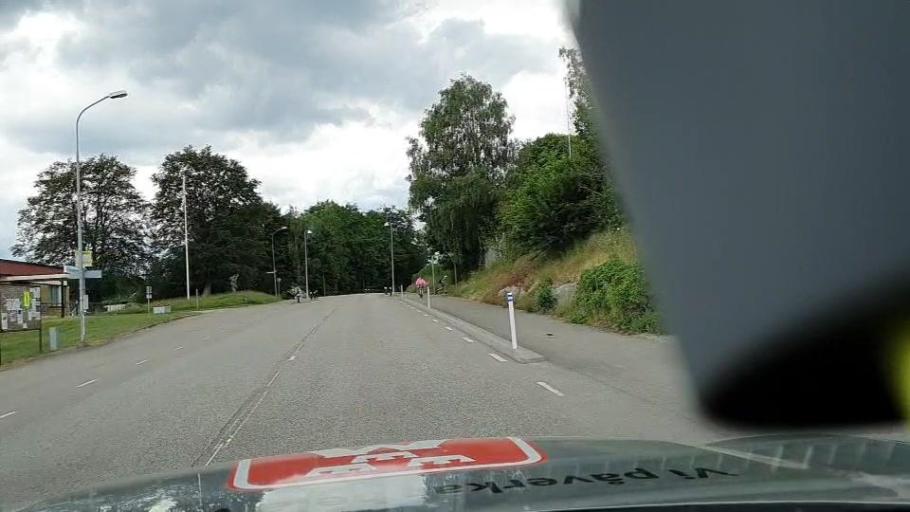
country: SE
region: Kalmar
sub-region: Emmaboda Kommun
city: Emmaboda
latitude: 56.5336
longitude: 15.5832
